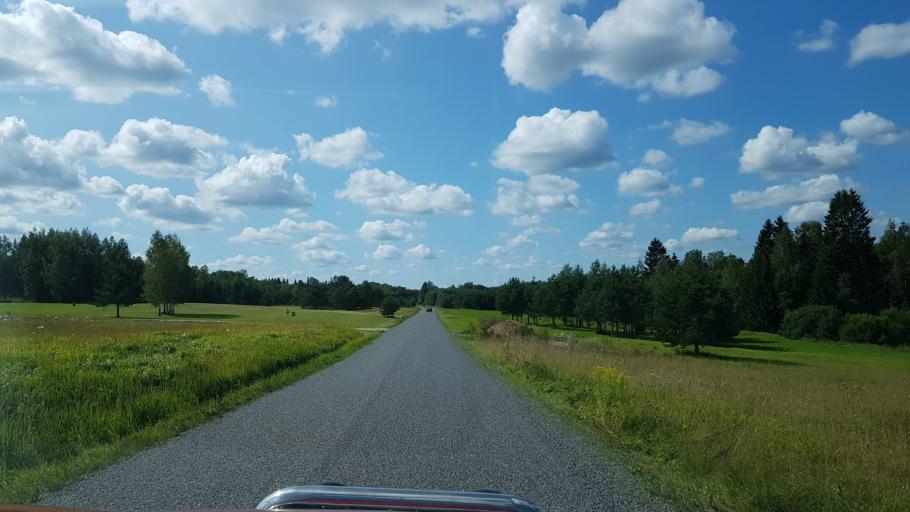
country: EE
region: Vorumaa
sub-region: Voru linn
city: Voru
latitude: 57.7294
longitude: 27.2314
